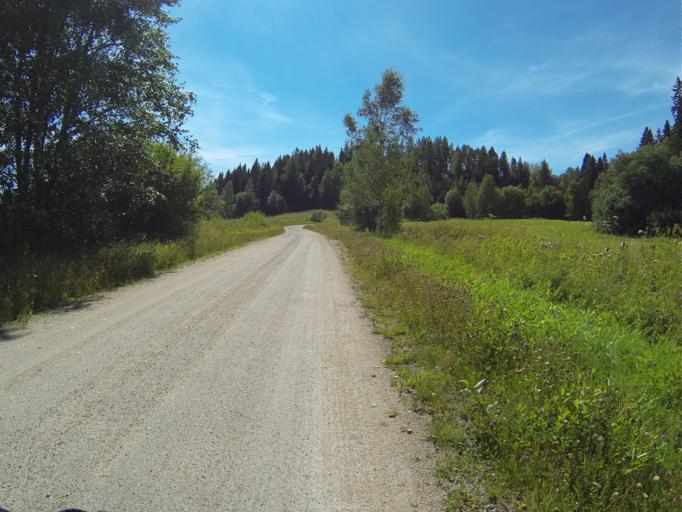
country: FI
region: Varsinais-Suomi
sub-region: Salo
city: Salo
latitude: 60.3024
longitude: 23.1066
